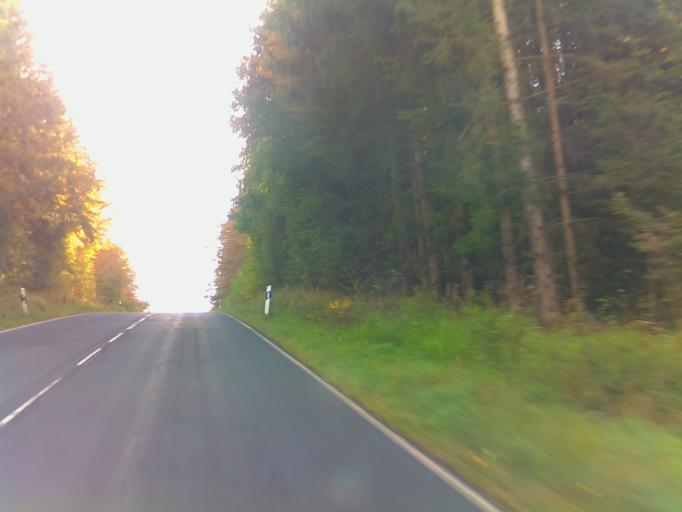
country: DE
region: Hesse
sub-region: Regierungsbezirk Darmstadt
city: Steinau an der Strasse
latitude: 50.3437
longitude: 9.3990
